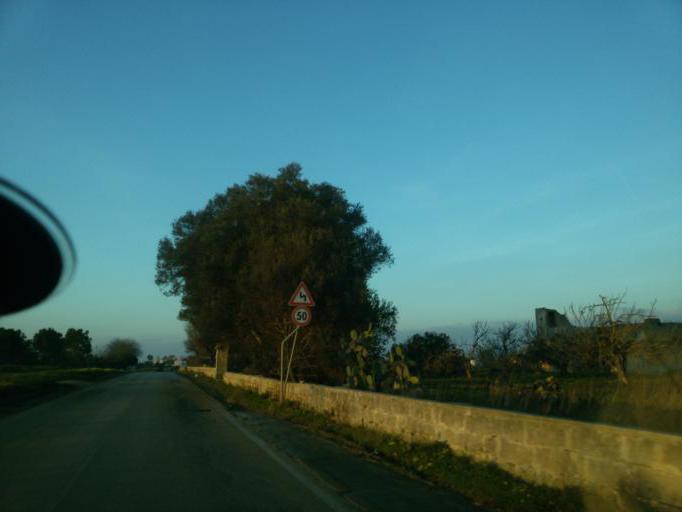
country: IT
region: Apulia
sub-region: Provincia di Brindisi
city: La Rosa
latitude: 40.6024
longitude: 17.9462
